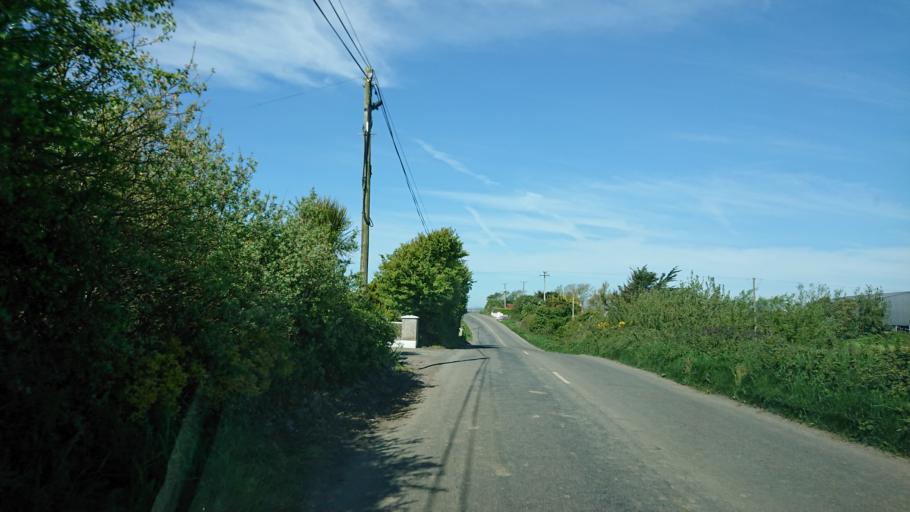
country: IE
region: Munster
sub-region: Waterford
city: Dunmore East
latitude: 52.1701
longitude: -7.0593
